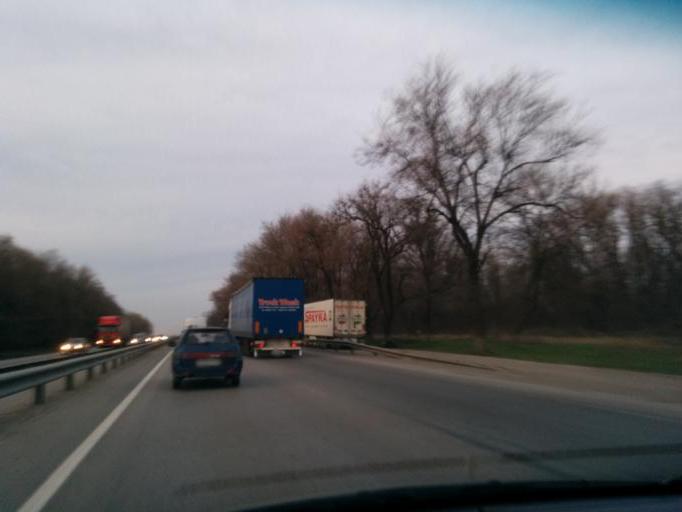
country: RU
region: Rostov
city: Aksay
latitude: 47.2955
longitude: 39.8578
